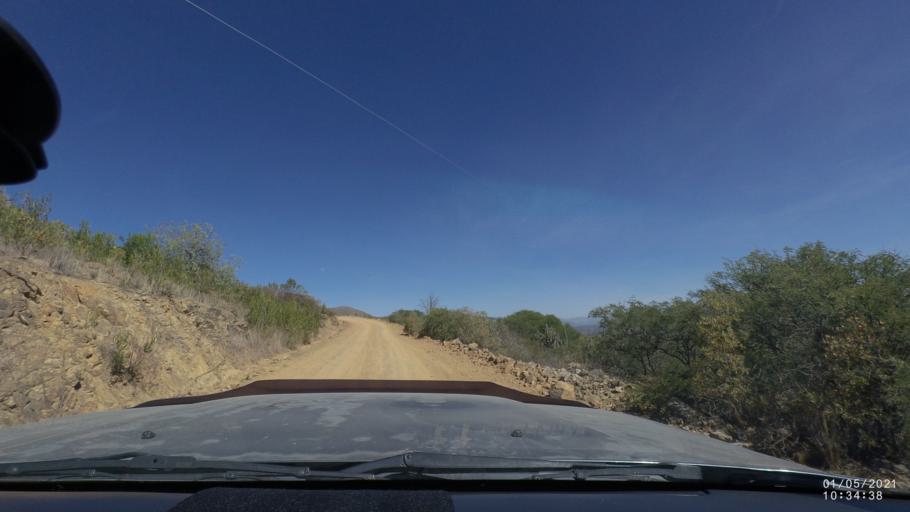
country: BO
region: Cochabamba
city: Capinota
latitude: -17.5972
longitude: -66.1902
